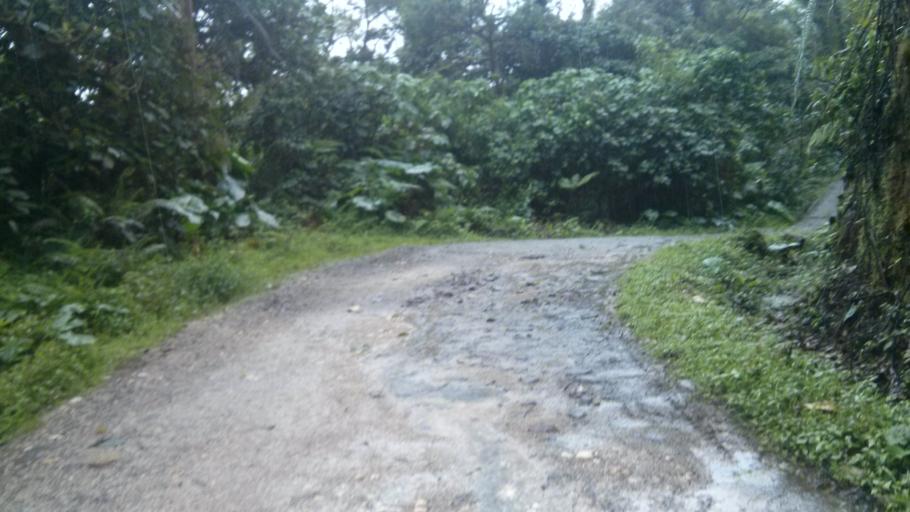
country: CR
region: San Jose
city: Ipis
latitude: 10.0297
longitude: -83.9420
